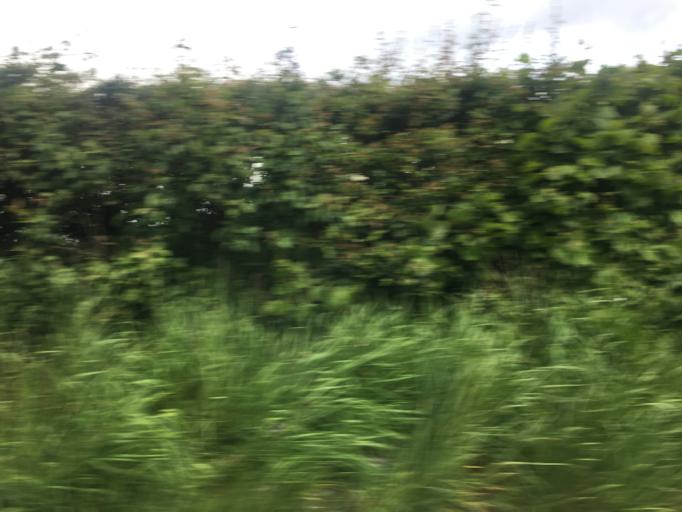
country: GB
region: Wales
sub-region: County of Ceredigion
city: Lampeter
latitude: 52.1333
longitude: -4.0727
